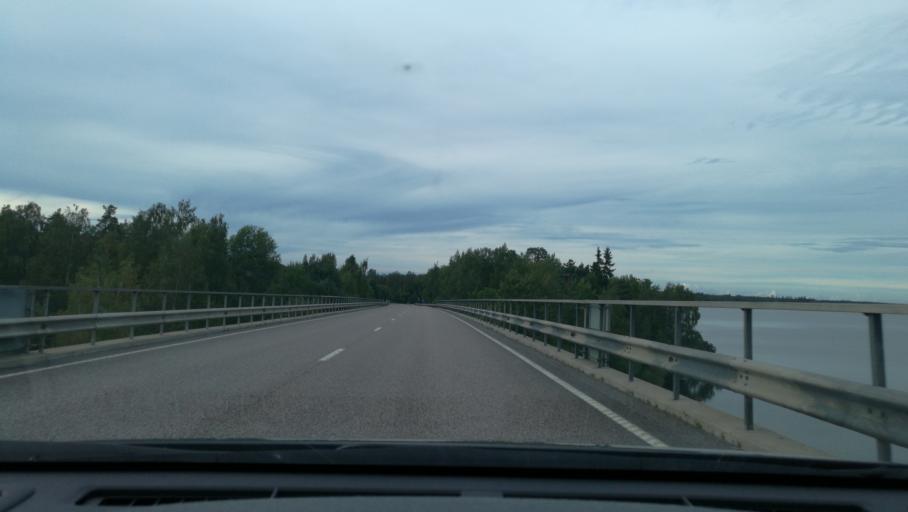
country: SE
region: Vaestmanland
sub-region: Kungsors Kommun
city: Kungsoer
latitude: 59.2362
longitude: 16.1016
